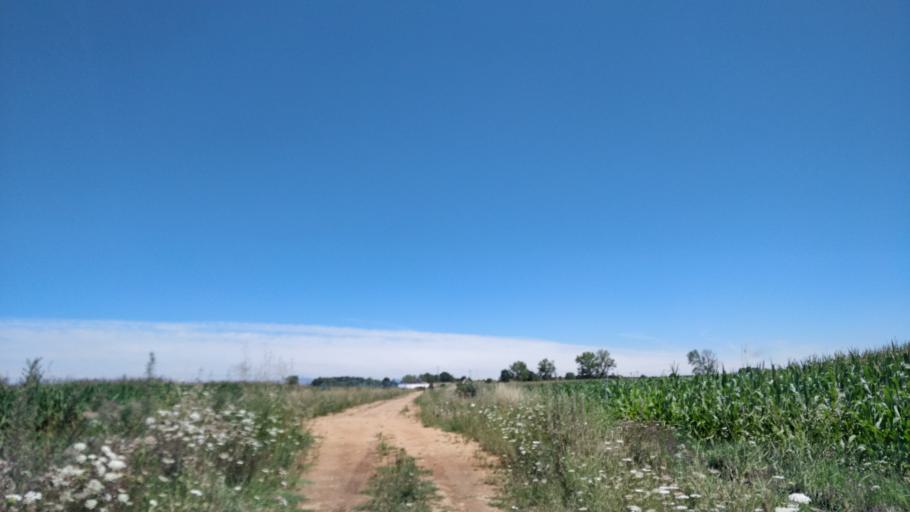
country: ES
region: Castille and Leon
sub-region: Provincia de Leon
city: Bustillo del Paramo
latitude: 42.4715
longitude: -5.8128
